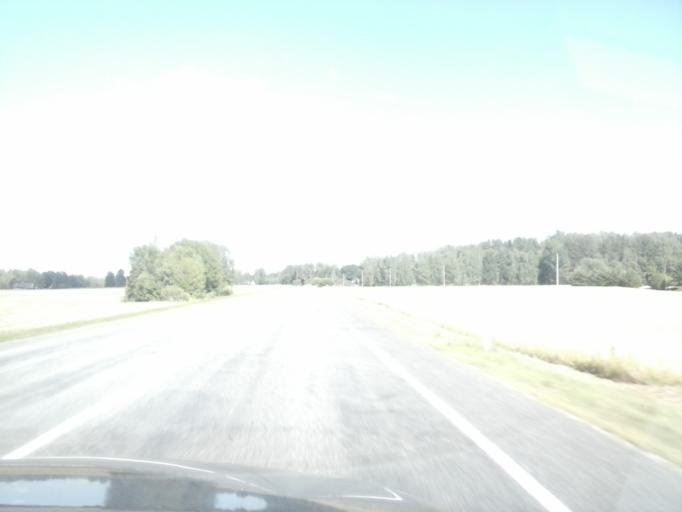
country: LV
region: Apes Novads
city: Ape
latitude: 57.6604
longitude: 26.7050
